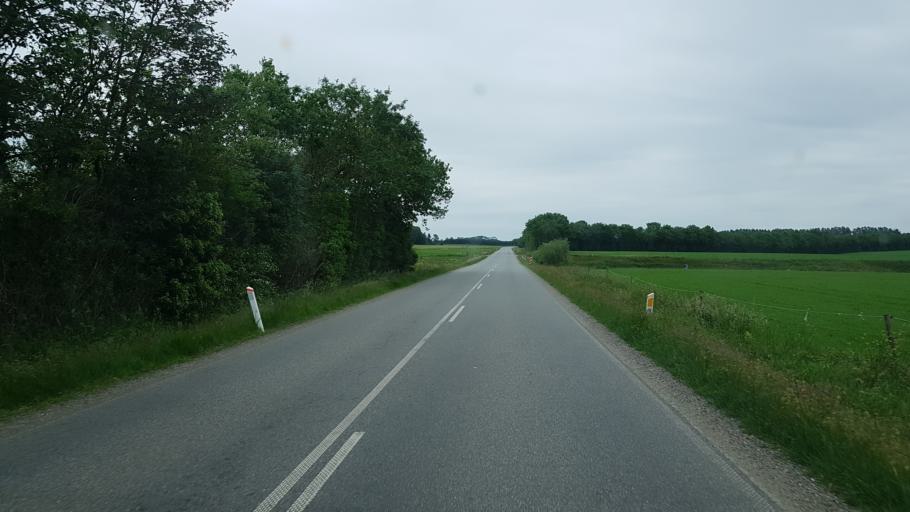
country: DK
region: South Denmark
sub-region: Varde Kommune
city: Olgod
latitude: 55.7110
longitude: 8.6956
